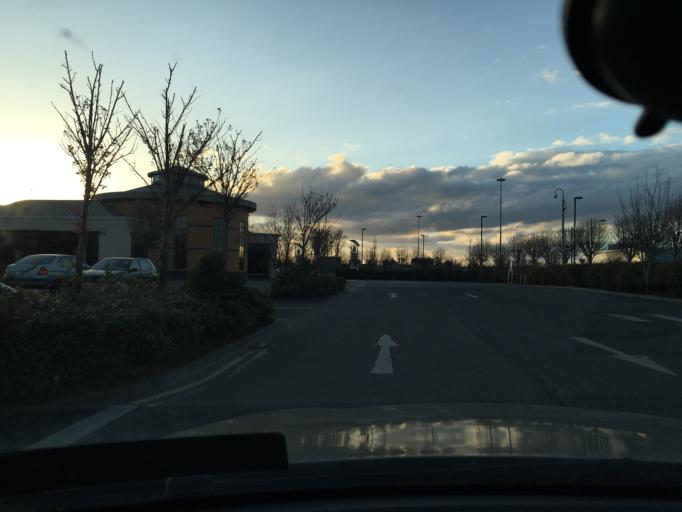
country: IE
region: Leinster
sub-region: Fingal County
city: Blanchardstown
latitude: 53.3924
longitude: -6.3934
